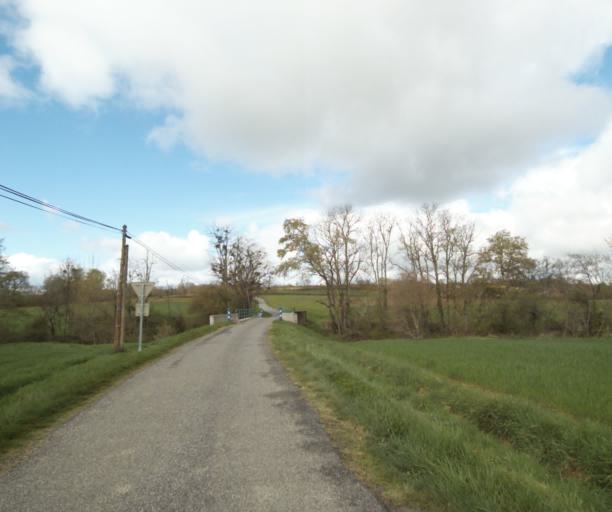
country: FR
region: Midi-Pyrenees
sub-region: Departement de l'Ariege
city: Saverdun
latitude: 43.2327
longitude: 1.5625
